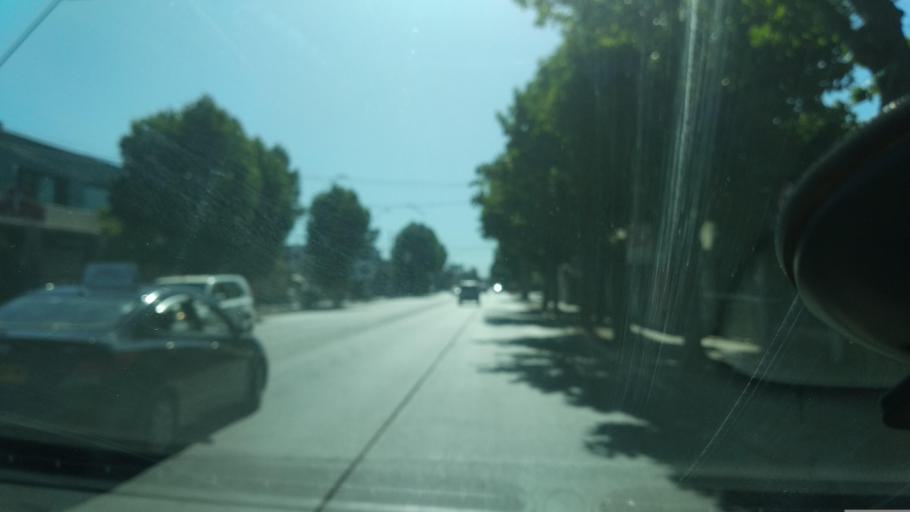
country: CL
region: Valparaiso
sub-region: Provincia de Marga Marga
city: Villa Alemana
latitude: -33.0443
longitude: -71.3790
